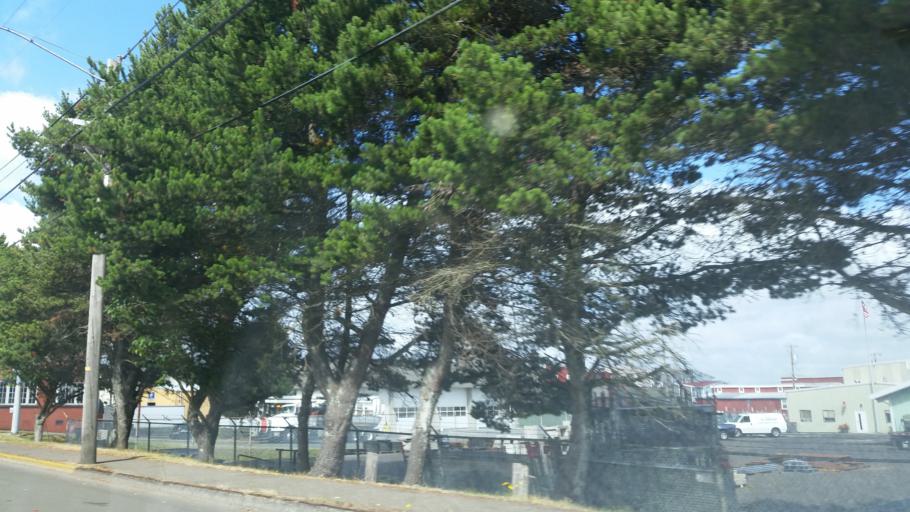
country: US
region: Oregon
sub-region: Clatsop County
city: Astoria
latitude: 46.1907
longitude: -123.8102
